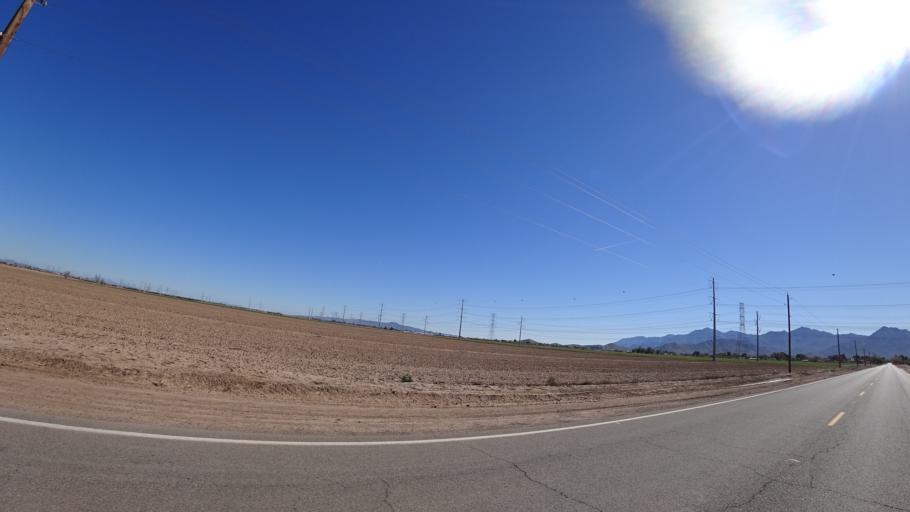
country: US
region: Arizona
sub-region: Maricopa County
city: Avondale
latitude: 33.4042
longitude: -112.3405
